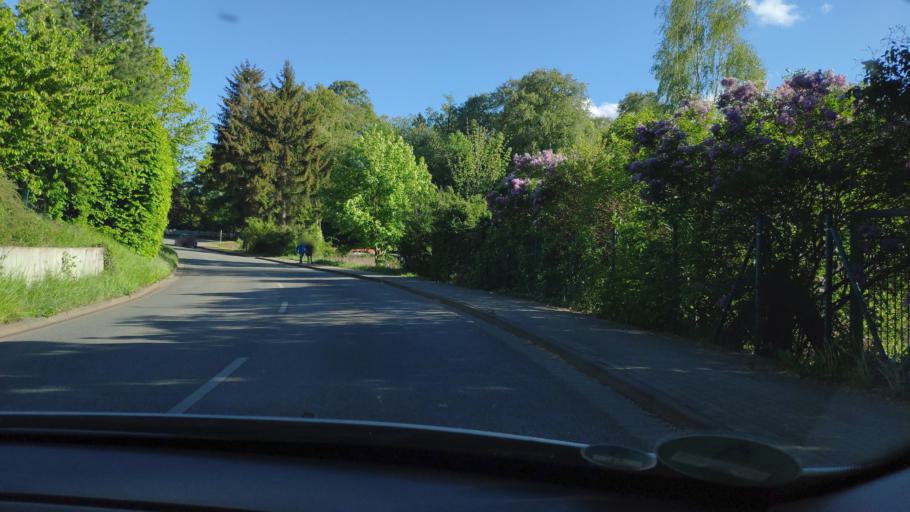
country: DE
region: Mecklenburg-Vorpommern
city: Neustrelitz
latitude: 53.3551
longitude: 13.0512
